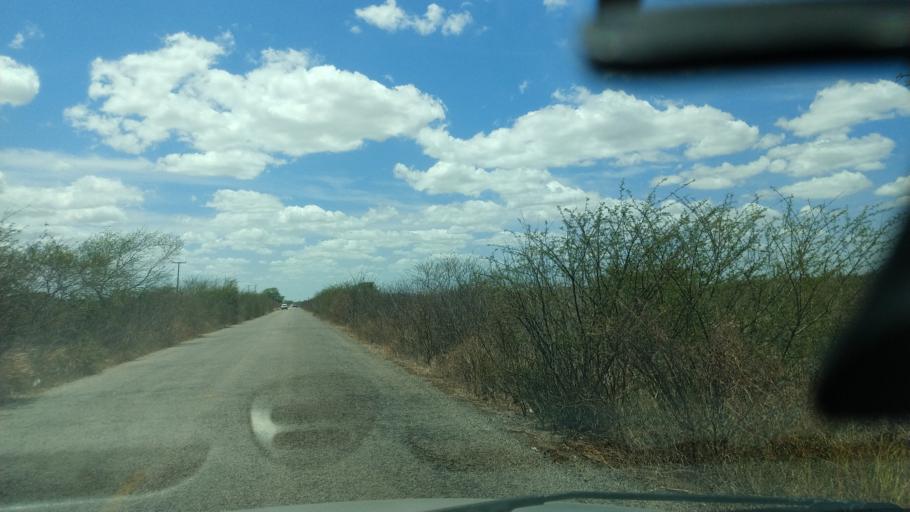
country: BR
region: Rio Grande do Norte
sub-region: Sao Paulo Do Potengi
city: Sao Paulo do Potengi
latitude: -5.9155
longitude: -35.7606
